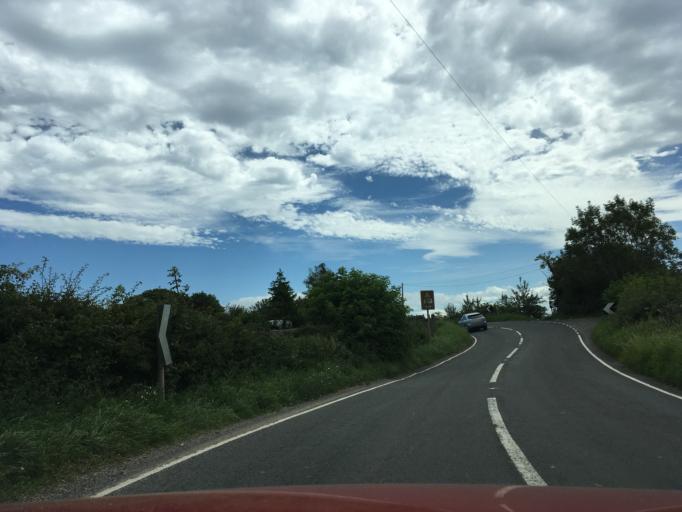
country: GB
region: England
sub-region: Somerset
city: Bradley Cross
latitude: 51.2441
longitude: -2.7332
